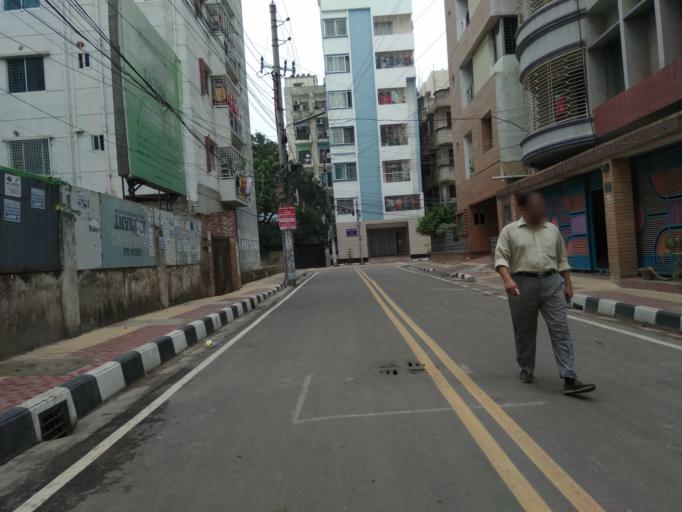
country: BD
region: Dhaka
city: Tungi
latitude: 23.8239
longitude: 90.3630
